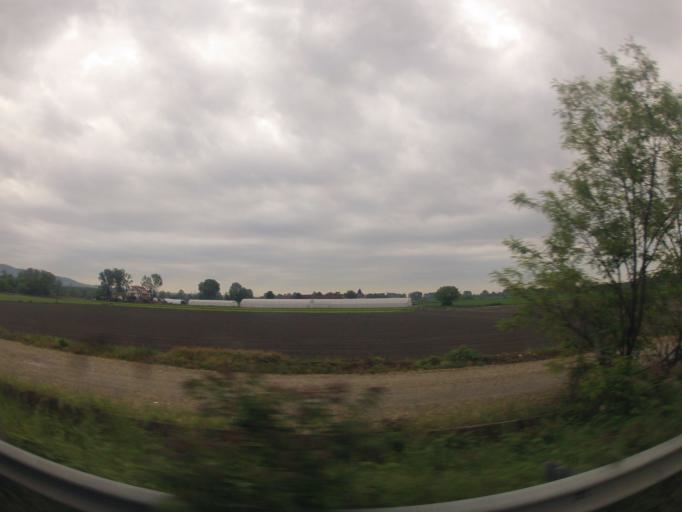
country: IT
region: Piedmont
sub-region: Provincia di Torino
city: La Loggia
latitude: 44.9590
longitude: 7.6807
